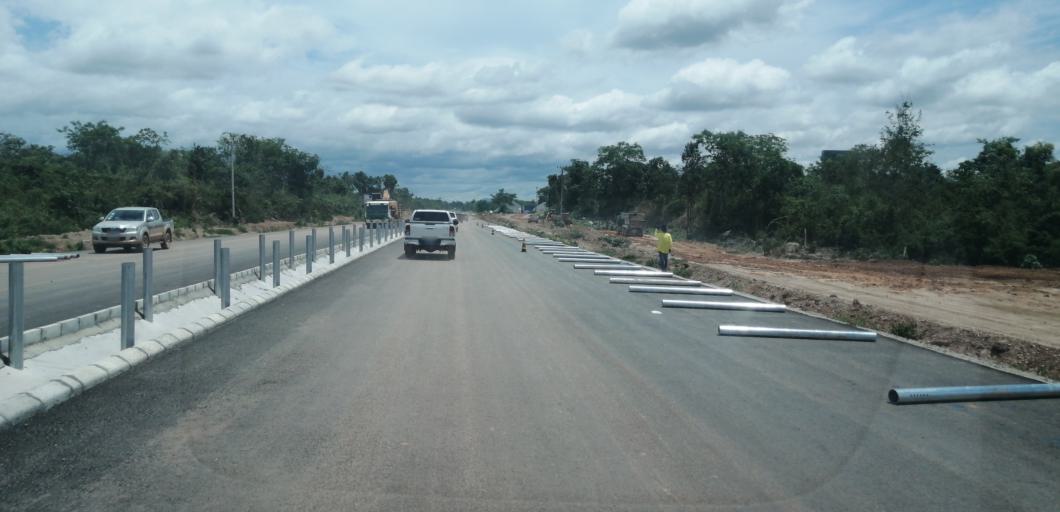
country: LA
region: Vientiane
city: Muang Phon-Hong
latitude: 18.2949
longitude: 102.4572
